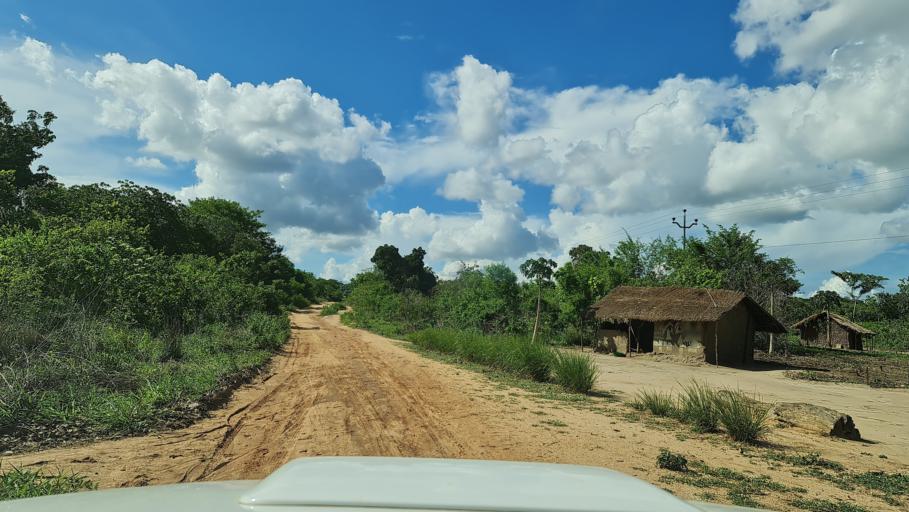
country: MZ
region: Nampula
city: Ilha de Mocambique
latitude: -15.4232
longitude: 40.2683
